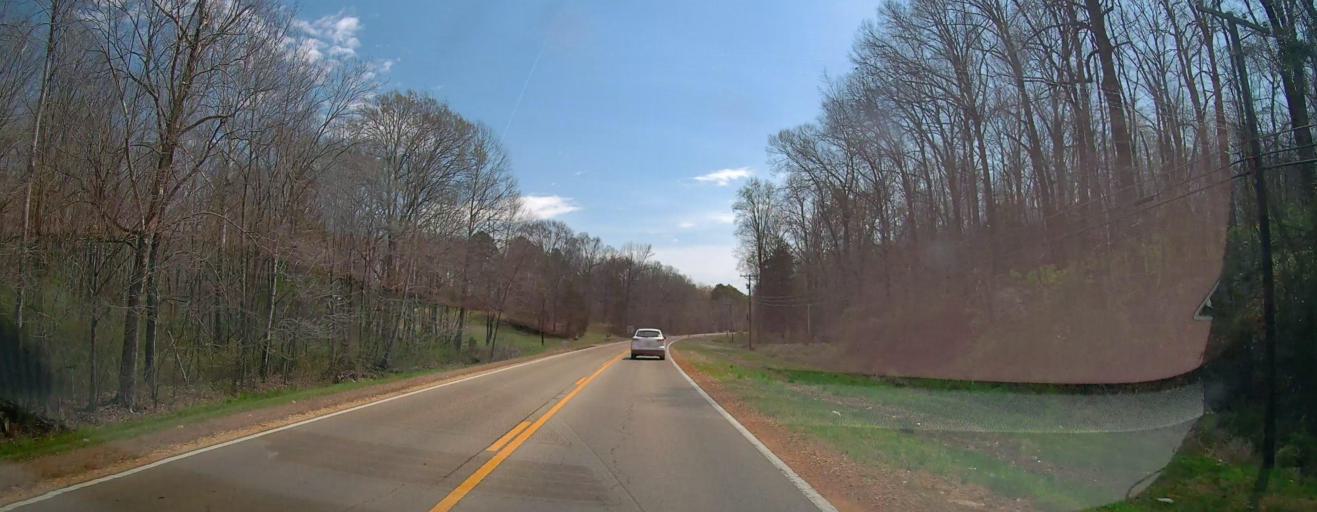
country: US
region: Mississippi
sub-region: Union County
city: New Albany
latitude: 34.4678
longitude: -88.9863
